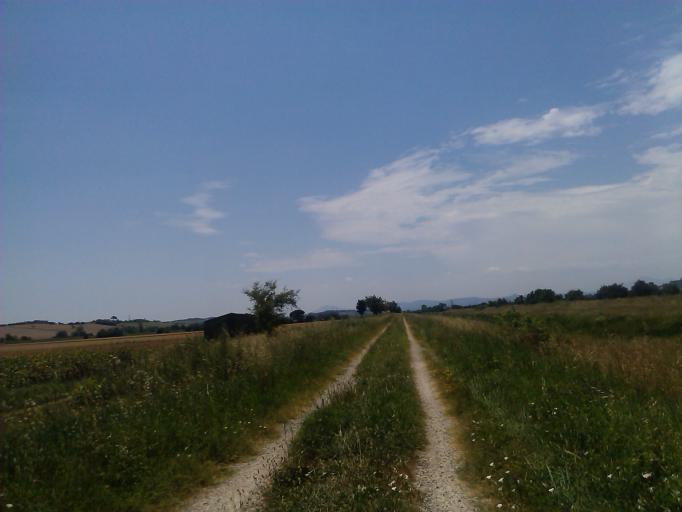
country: IT
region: Tuscany
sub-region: Province of Arezzo
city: Cesa
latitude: 43.2887
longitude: 11.8415
